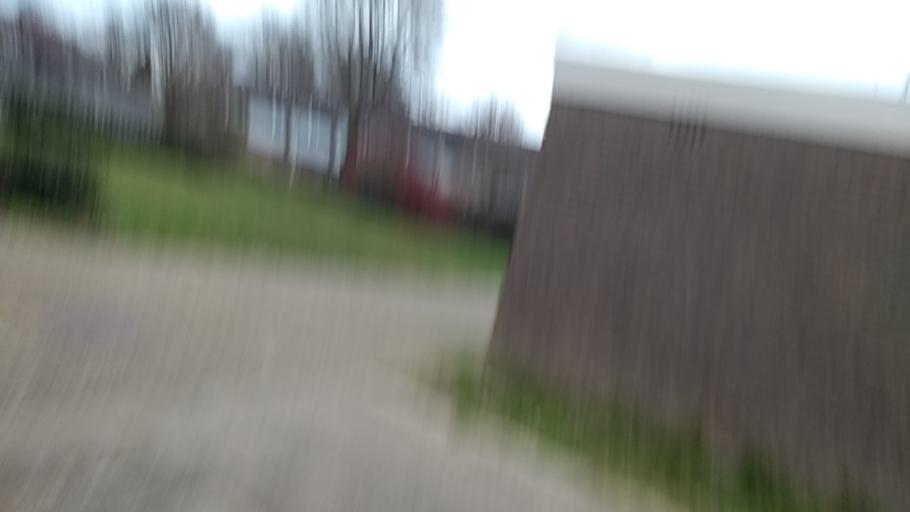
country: NL
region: Overijssel
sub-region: Gemeente Almelo
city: Almelo
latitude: 52.3758
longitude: 6.6728
